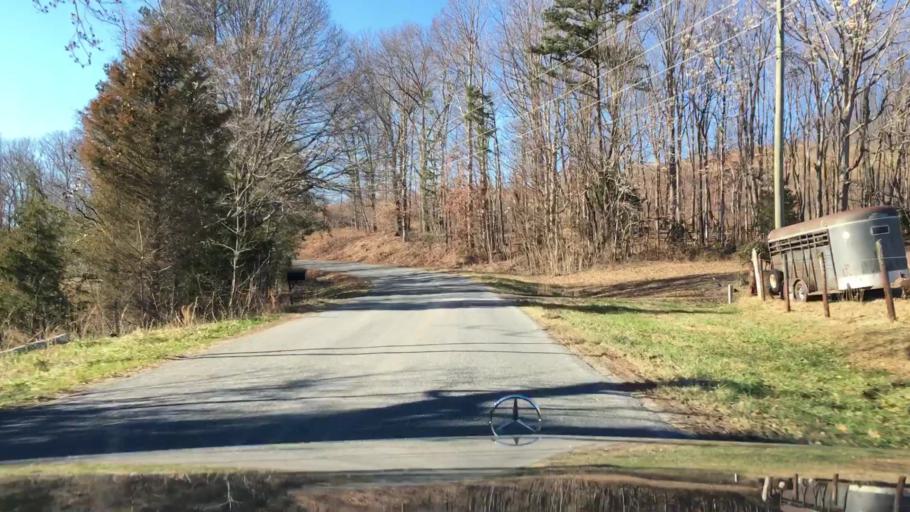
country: US
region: Virginia
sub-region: Campbell County
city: Altavista
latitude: 37.1660
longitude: -79.3585
